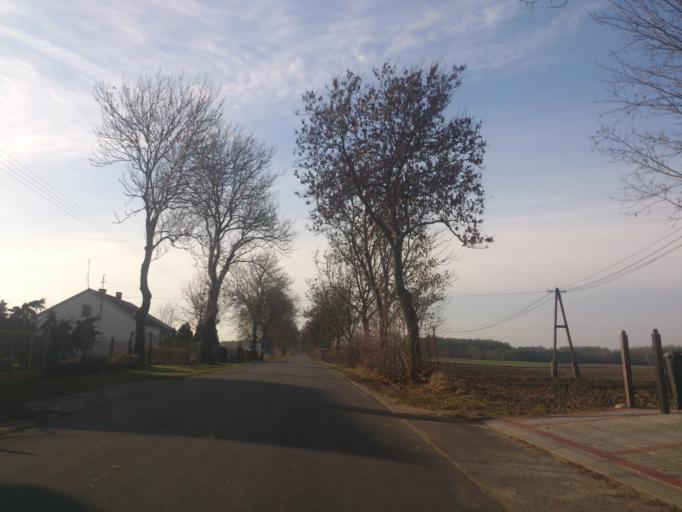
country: PL
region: Kujawsko-Pomorskie
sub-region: Powiat golubsko-dobrzynski
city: Radomin
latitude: 53.1097
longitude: 19.1436
